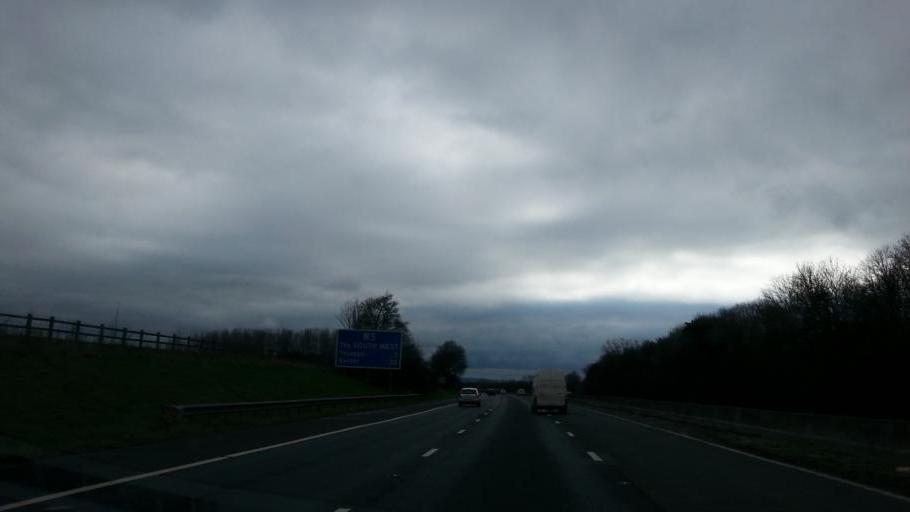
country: GB
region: England
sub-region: Somerset
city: North Petherton
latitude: 51.0938
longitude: -3.0017
